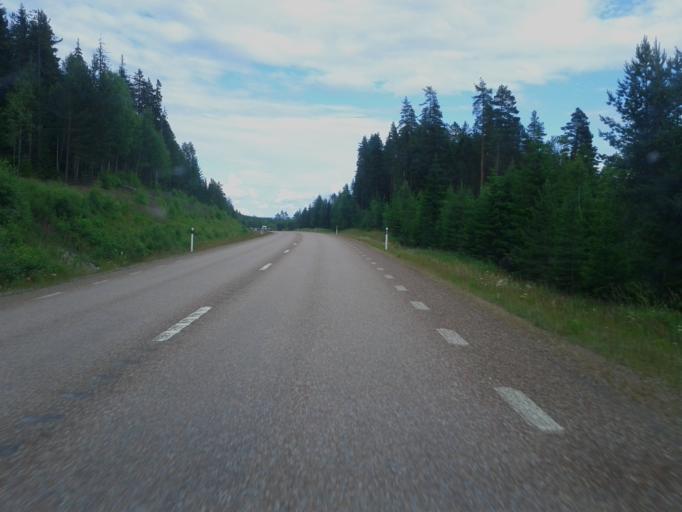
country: SE
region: Dalarna
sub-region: Faluns Kommun
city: Bjursas
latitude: 60.7457
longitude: 15.3709
